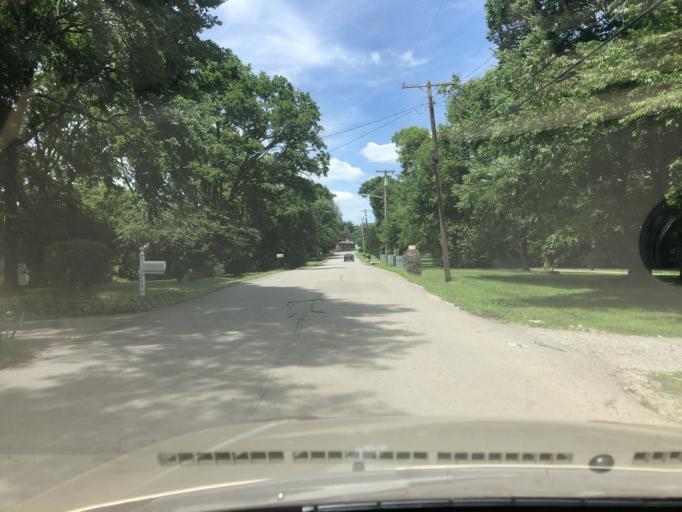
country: US
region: Tennessee
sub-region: Davidson County
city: Lakewood
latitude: 36.2520
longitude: -86.7014
